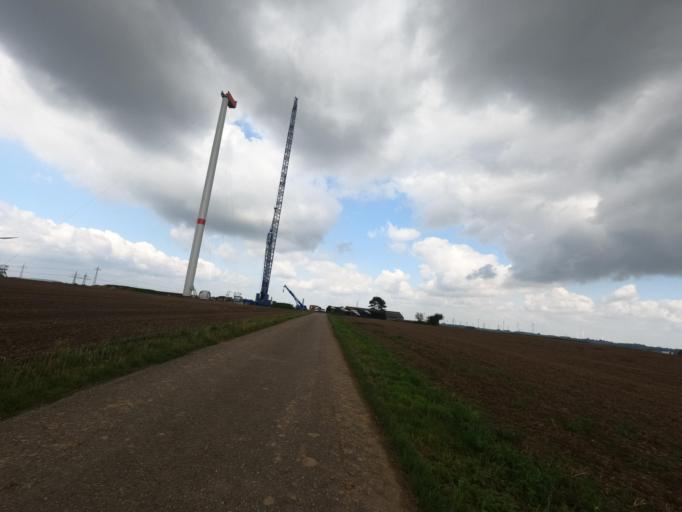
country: DE
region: North Rhine-Westphalia
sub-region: Regierungsbezirk Koln
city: Linnich
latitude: 50.9812
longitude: 6.2431
